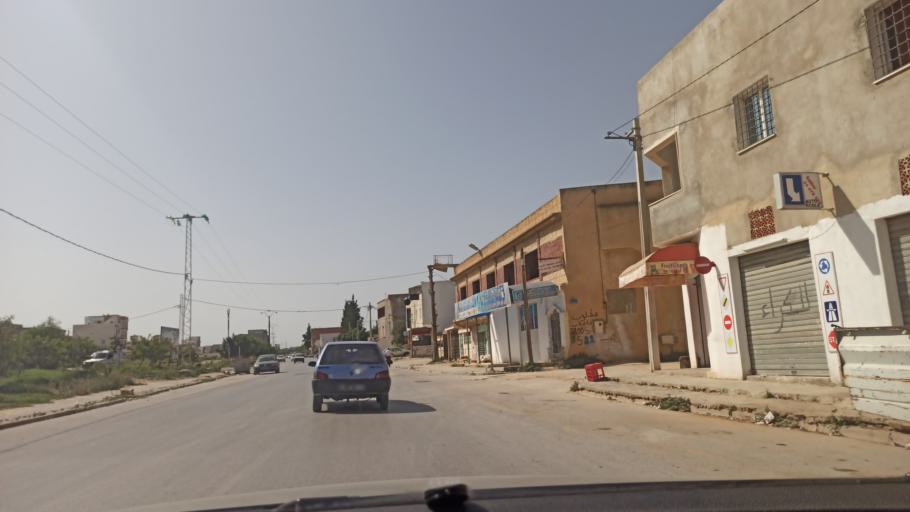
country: TN
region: Manouba
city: Manouba
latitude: 36.7568
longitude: 10.1035
